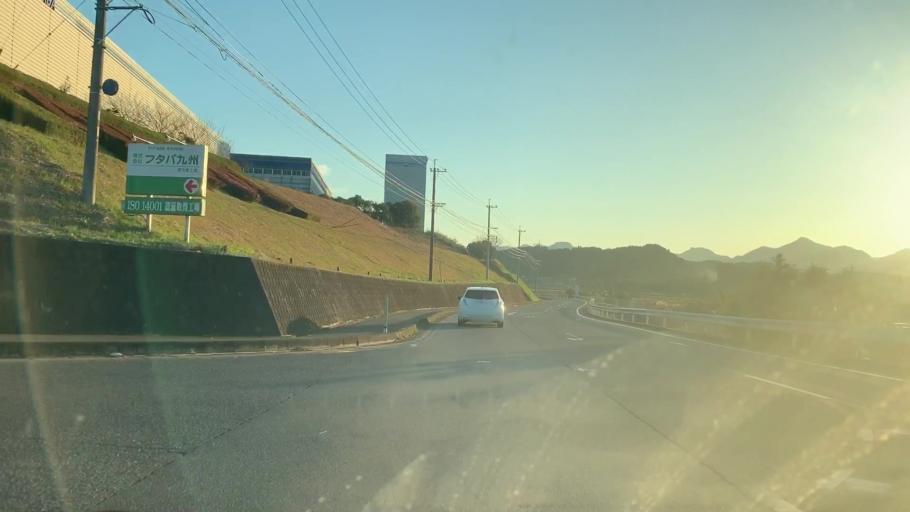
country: JP
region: Saga Prefecture
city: Imaricho-ko
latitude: 33.2798
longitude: 129.9666
